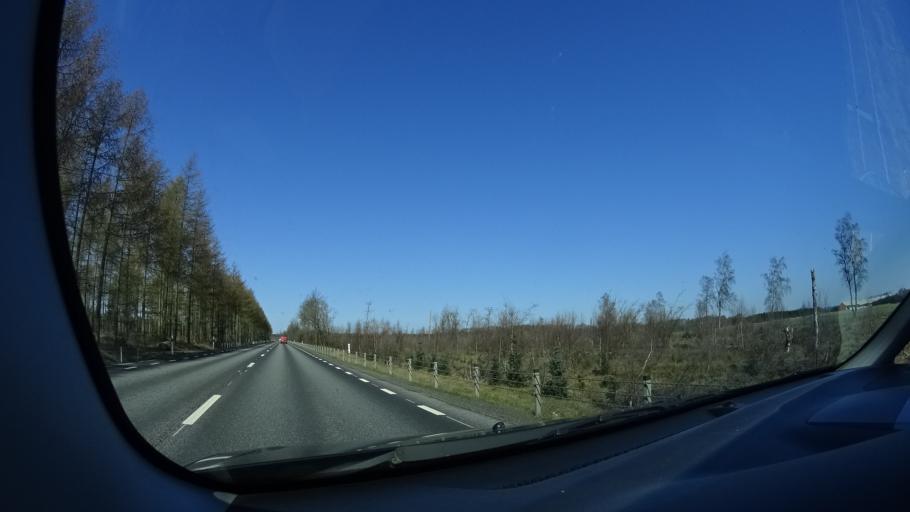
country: SE
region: Skane
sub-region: Angelholms Kommun
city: Strovelstorp
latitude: 56.1972
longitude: 12.8349
